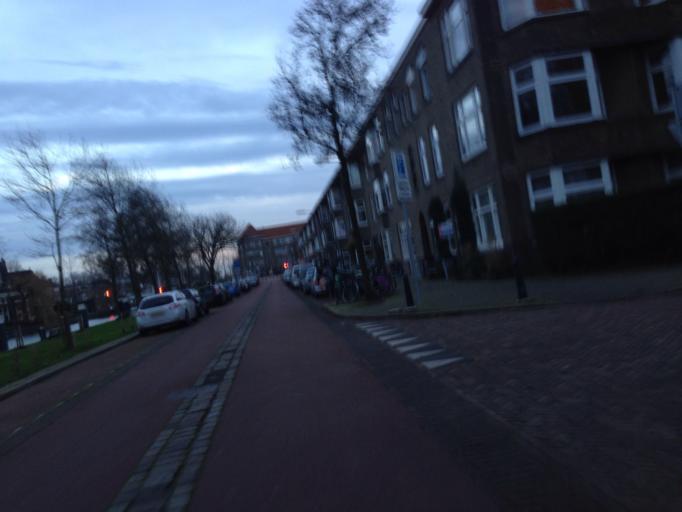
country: NL
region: South Holland
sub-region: Gemeente Leidschendam-Voorburg
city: Voorburg
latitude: 52.0606
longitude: 4.3421
